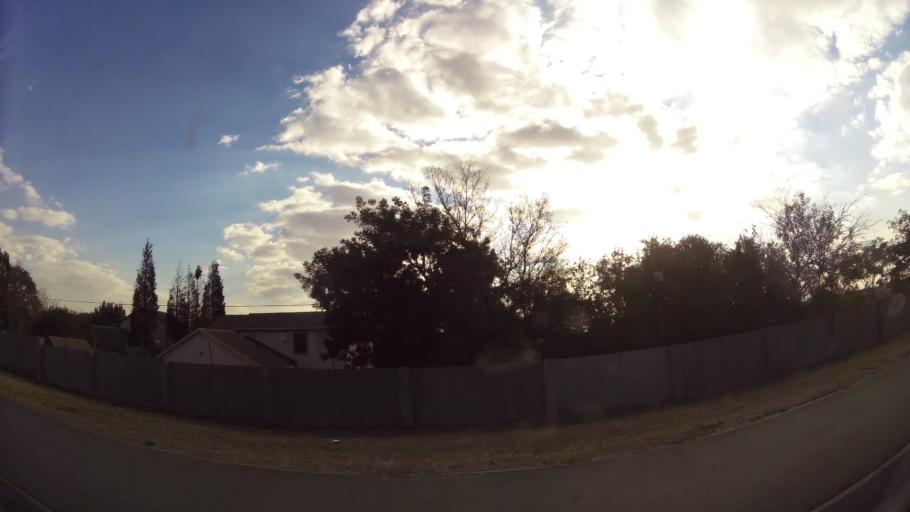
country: ZA
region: Gauteng
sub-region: City of Johannesburg Metropolitan Municipality
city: Diepsloot
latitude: -26.0100
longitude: 28.0113
